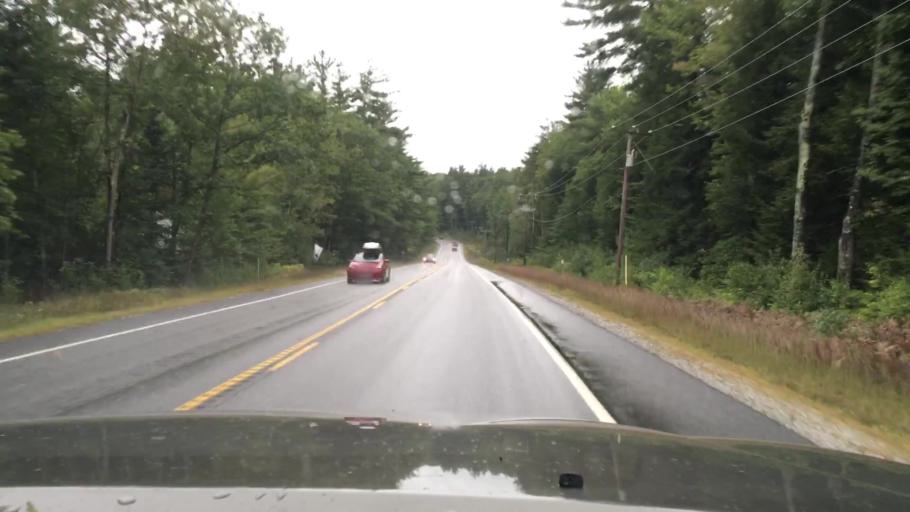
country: US
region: New Hampshire
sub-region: Hillsborough County
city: Antrim
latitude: 43.0944
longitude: -71.9651
